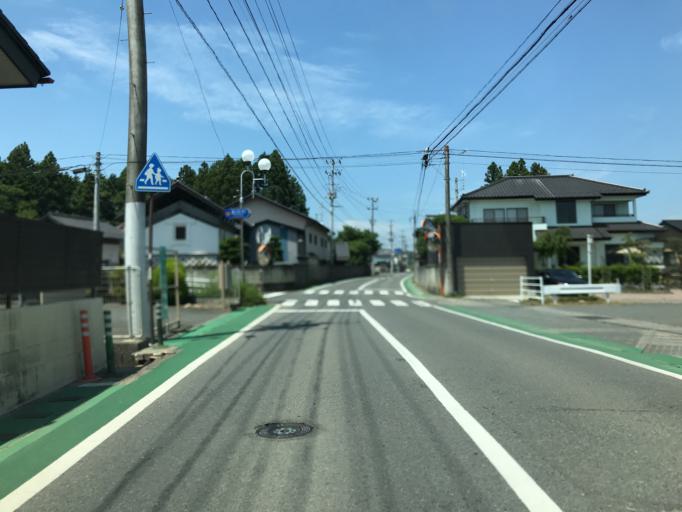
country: JP
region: Fukushima
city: Namie
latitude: 37.7206
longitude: 140.9294
